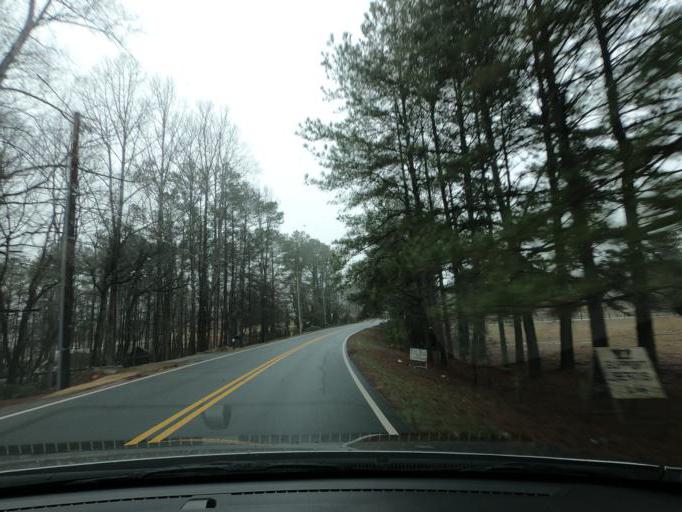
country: US
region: Georgia
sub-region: Fulton County
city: Alpharetta
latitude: 34.0999
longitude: -84.3259
